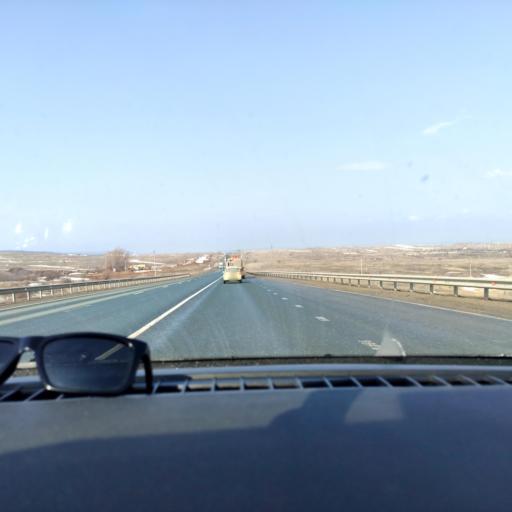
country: RU
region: Samara
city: Novosemeykino
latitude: 53.4000
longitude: 50.4095
